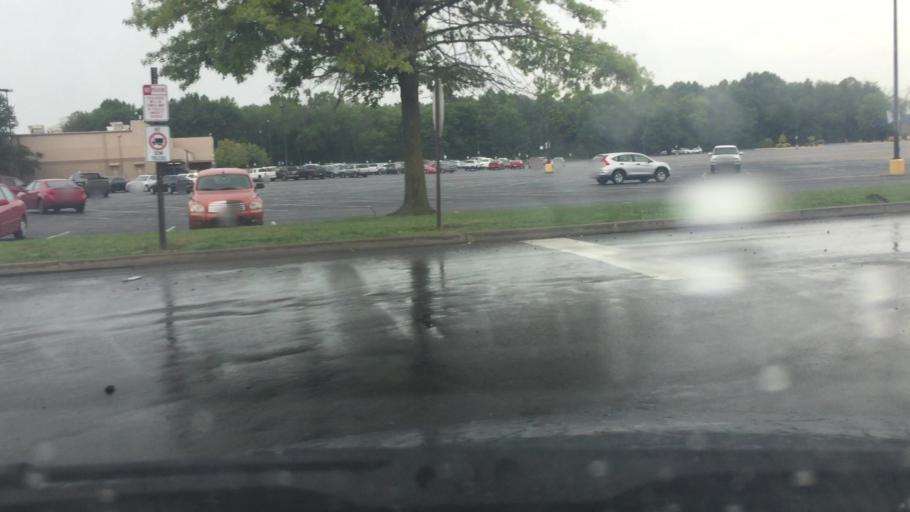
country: US
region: Illinois
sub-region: Williamson County
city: Marion
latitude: 37.7397
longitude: -88.9667
